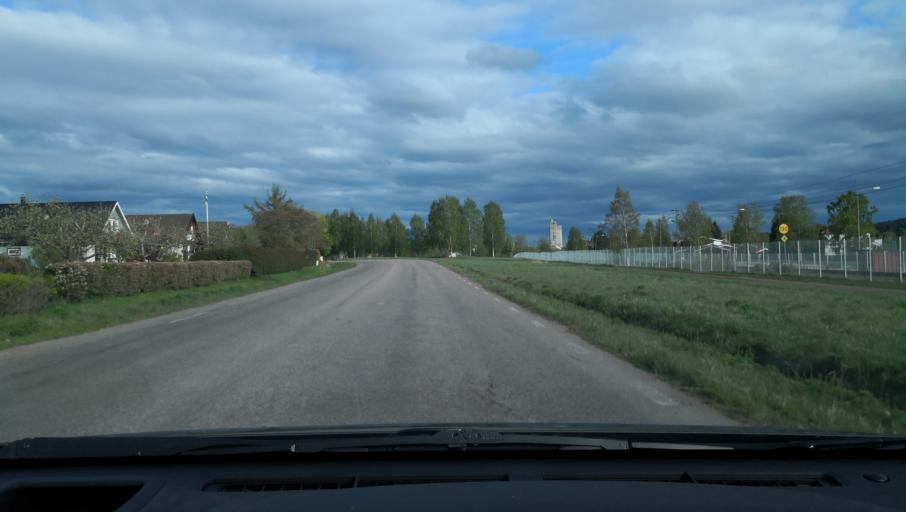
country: SE
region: Dalarna
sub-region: Hedemora Kommun
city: Hedemora
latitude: 60.2804
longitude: 15.9673
